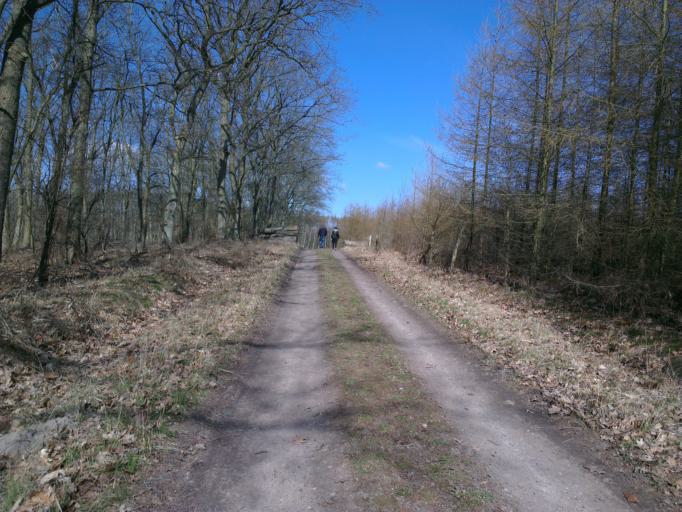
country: DK
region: Capital Region
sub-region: Frederikssund Kommune
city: Jaegerspris
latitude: 55.9093
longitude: 11.9416
